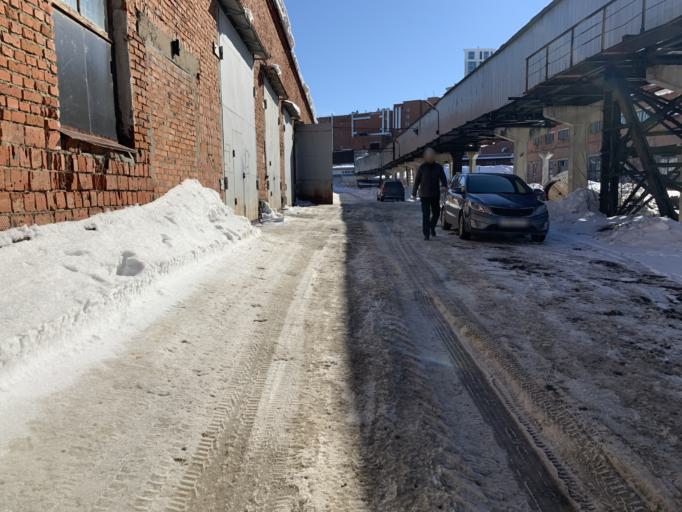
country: RU
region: Chuvashia
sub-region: Cheboksarskiy Rayon
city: Cheboksary
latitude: 56.1400
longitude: 47.2783
